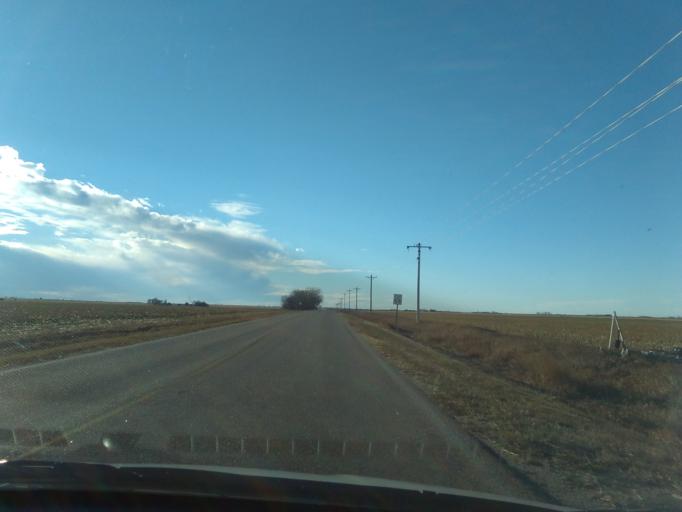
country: US
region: Nebraska
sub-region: Kearney County
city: Minden
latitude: 40.3651
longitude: -99.0661
